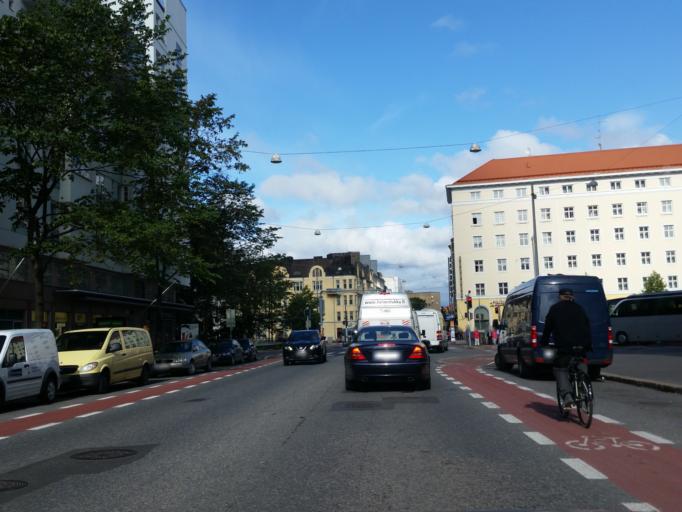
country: FI
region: Uusimaa
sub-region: Helsinki
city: Helsinki
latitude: 60.1690
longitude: 24.9283
